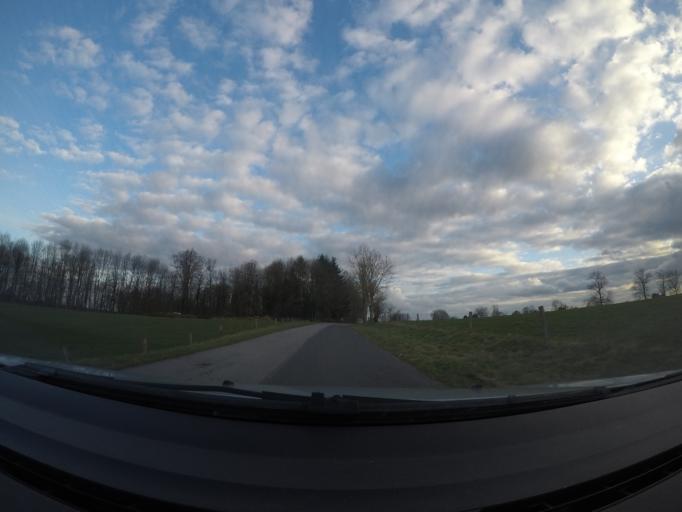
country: BE
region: Wallonia
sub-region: Province du Luxembourg
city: Etalle
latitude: 49.6798
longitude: 5.5652
